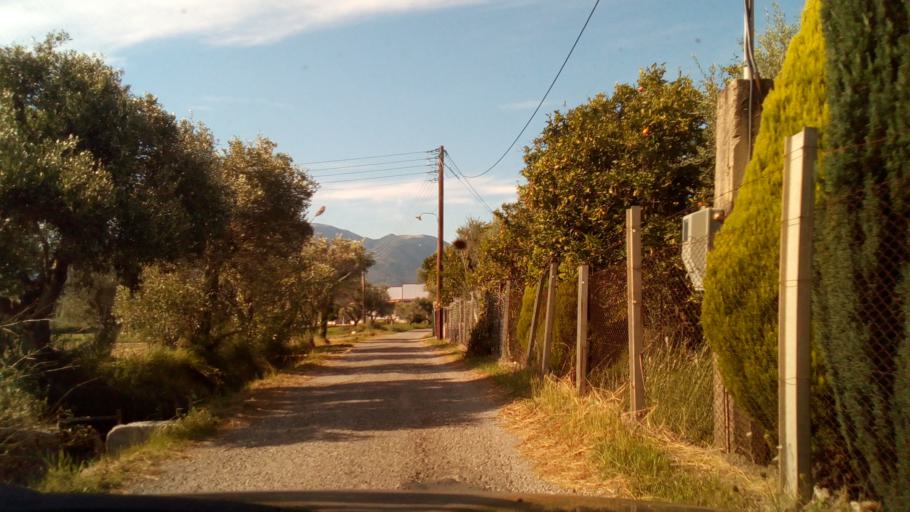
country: GR
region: West Greece
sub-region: Nomos Aitolias kai Akarnanias
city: Nafpaktos
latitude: 38.3984
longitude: 21.9022
